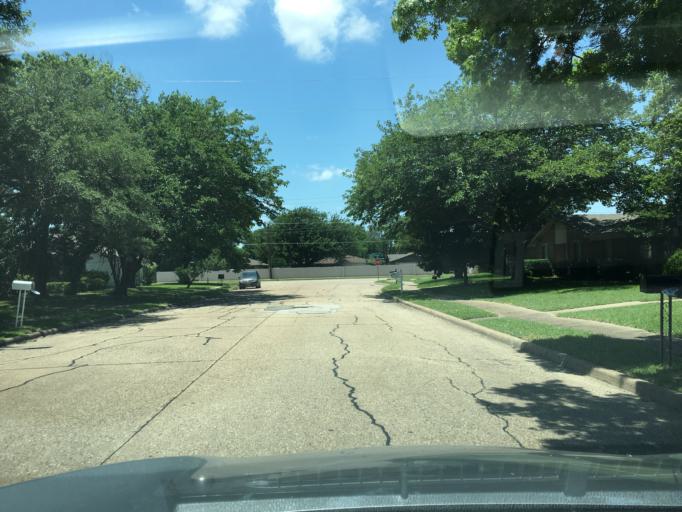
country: US
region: Texas
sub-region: Dallas County
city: Richardson
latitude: 32.9500
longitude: -96.6818
